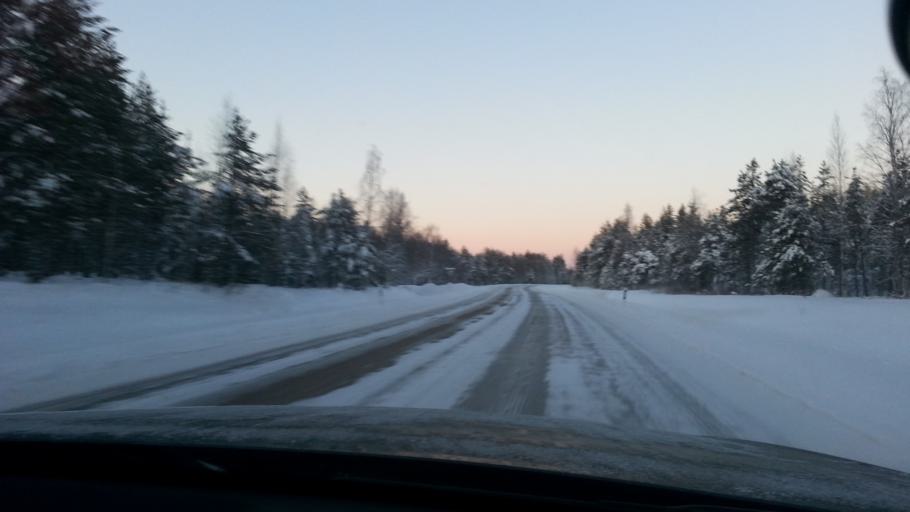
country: FI
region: Lapland
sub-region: Tunturi-Lappi
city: Kittilae
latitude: 67.0617
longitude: 25.0865
